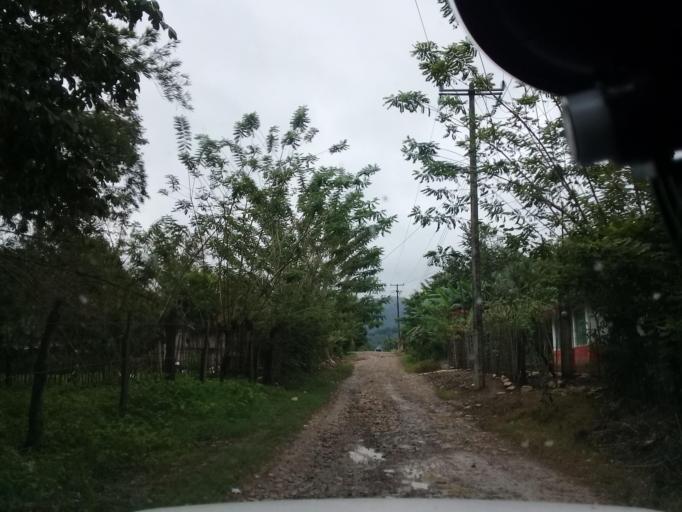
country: MX
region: Veracruz
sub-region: Chalma
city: San Pedro Coyutla
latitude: 21.2286
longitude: -98.4245
